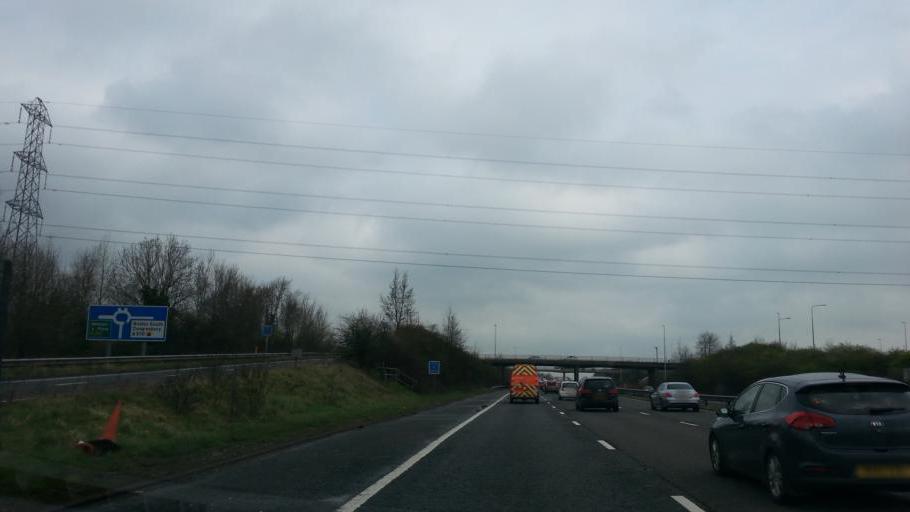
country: GB
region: England
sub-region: North Somerset
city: St. Georges
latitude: 51.3567
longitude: -2.8943
